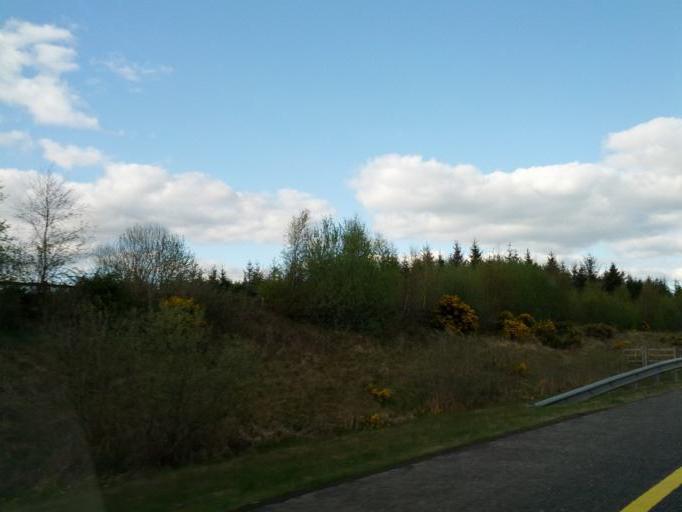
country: IE
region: Leinster
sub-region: An Iarmhi
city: Rochfortbridge
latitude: 53.4147
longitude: -7.2644
